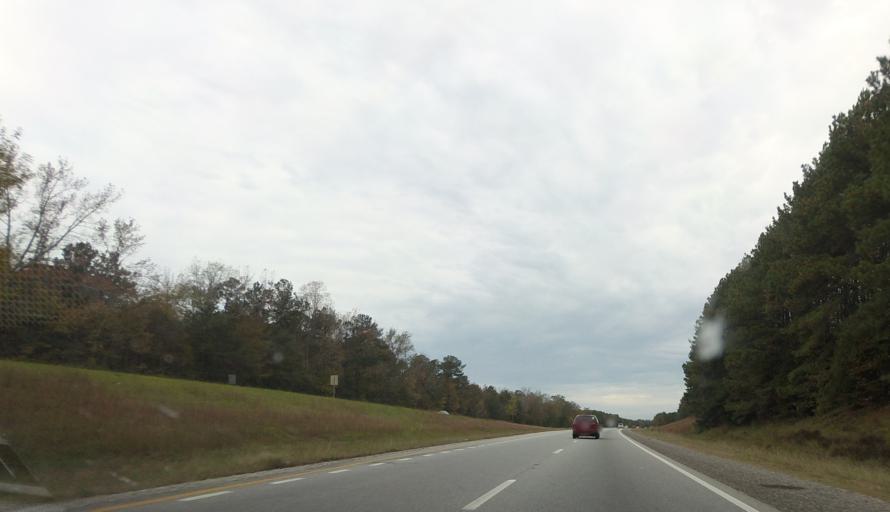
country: US
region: Alabama
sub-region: Lee County
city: Opelika
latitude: 32.6362
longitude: -85.3007
